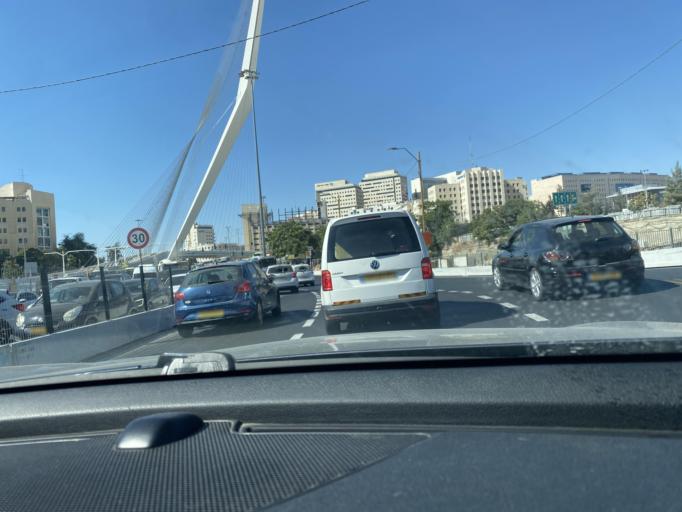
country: IL
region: Jerusalem
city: West Jerusalem
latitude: 31.7864
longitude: 35.1994
